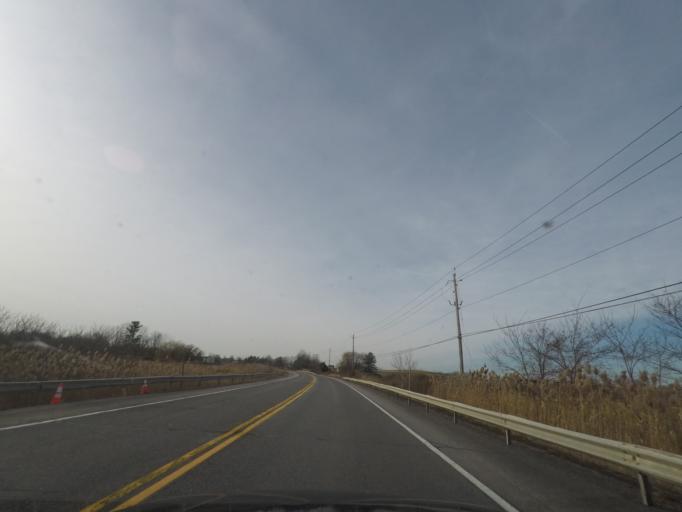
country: US
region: New York
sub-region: Saratoga County
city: Mechanicville
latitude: 42.8861
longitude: -73.7126
